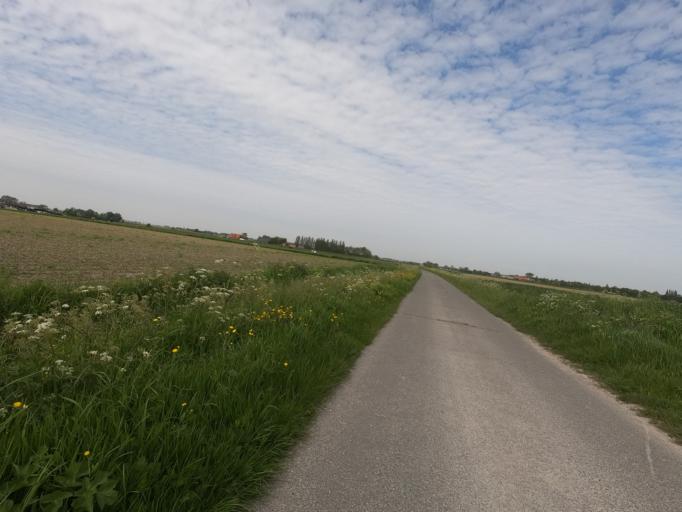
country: BE
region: Flanders
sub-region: Provincie West-Vlaanderen
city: Alveringem
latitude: 50.9694
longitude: 2.7149
